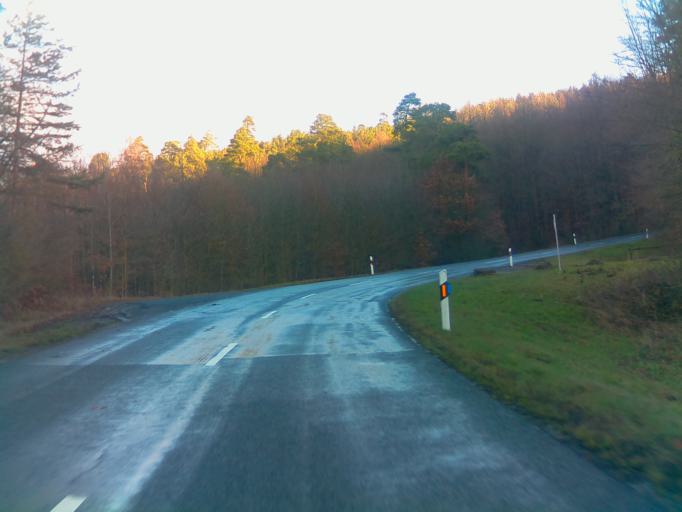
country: DE
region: Bavaria
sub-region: Regierungsbezirk Unterfranken
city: Sondheim vor der Rhoen
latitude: 50.4891
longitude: 10.1927
